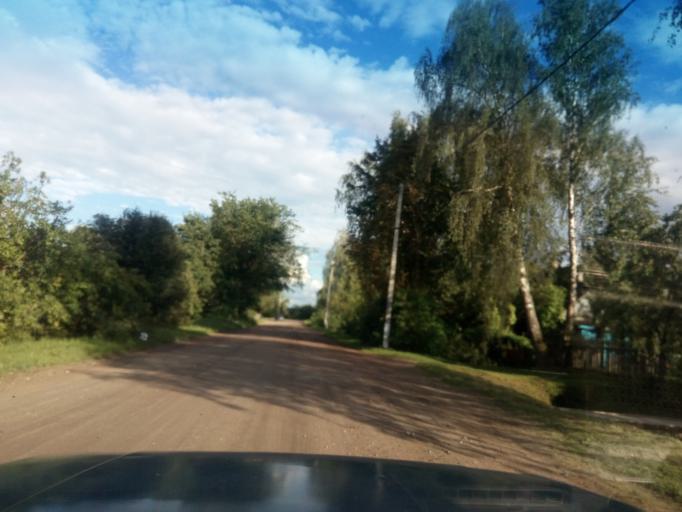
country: BY
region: Vitebsk
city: Dzisna
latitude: 55.6749
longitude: 28.3315
